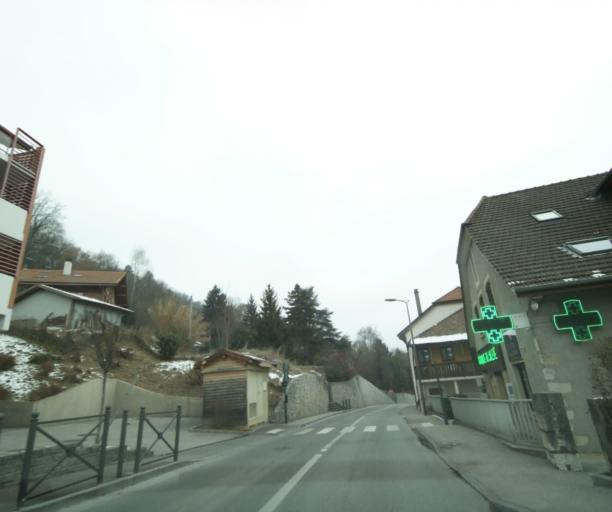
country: FR
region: Rhone-Alpes
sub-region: Departement de la Haute-Savoie
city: Vetraz-Monthoux
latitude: 46.1642
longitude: 6.2368
